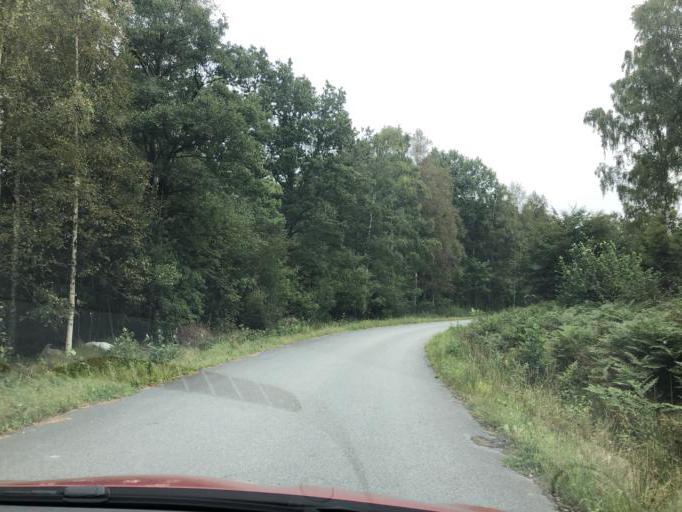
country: SE
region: Blekinge
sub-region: Solvesborgs Kommun
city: Soelvesborg
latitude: 56.1411
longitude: 14.5853
